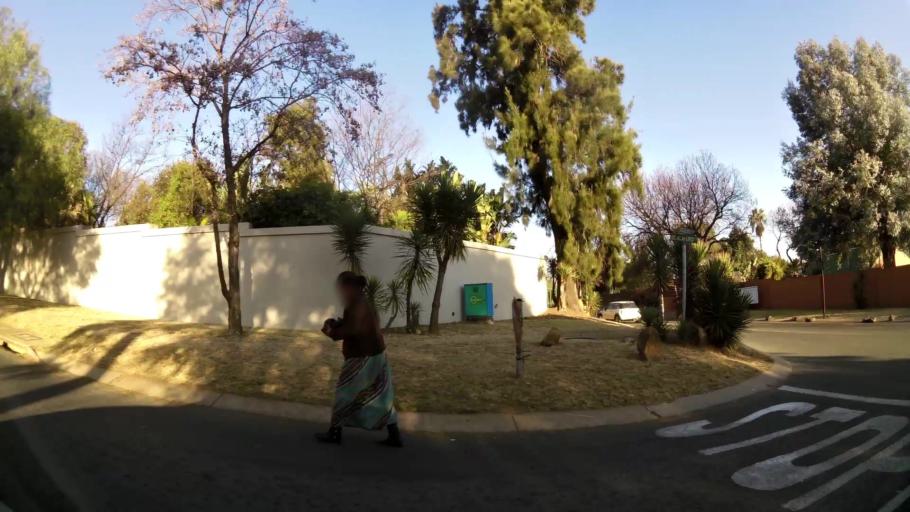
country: ZA
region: Gauteng
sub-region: City of Johannesburg Metropolitan Municipality
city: Modderfontein
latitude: -26.0738
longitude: 28.0756
